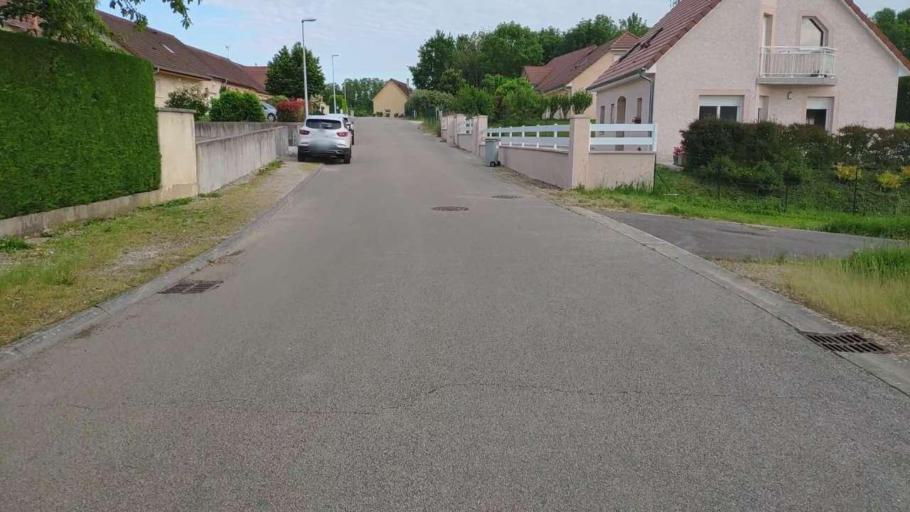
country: FR
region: Franche-Comte
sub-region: Departement du Jura
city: Bletterans
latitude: 46.7506
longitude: 5.4470
